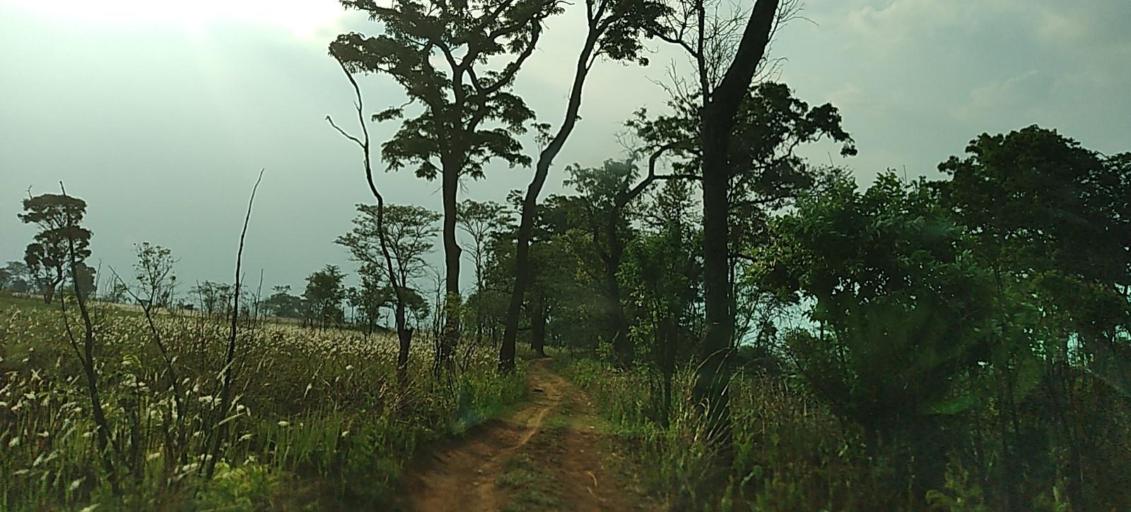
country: ZM
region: North-Western
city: Solwezi
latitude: -12.0459
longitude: 26.0592
